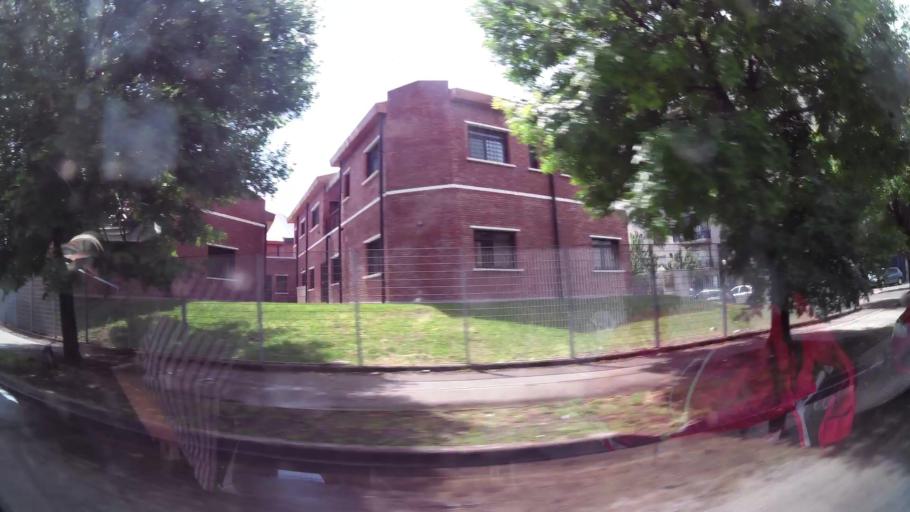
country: AR
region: Buenos Aires F.D.
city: Villa Lugano
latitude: -34.6638
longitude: -58.4687
